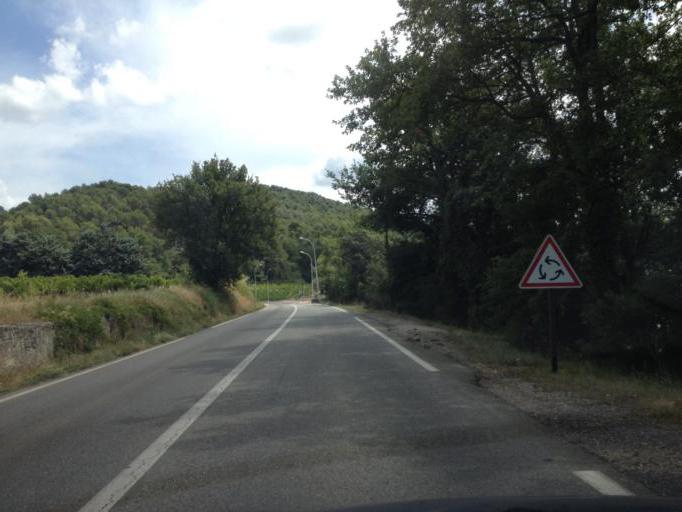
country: FR
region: Provence-Alpes-Cote d'Azur
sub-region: Departement du Vaucluse
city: Vaison-la-Romaine
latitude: 44.2458
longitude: 5.0479
